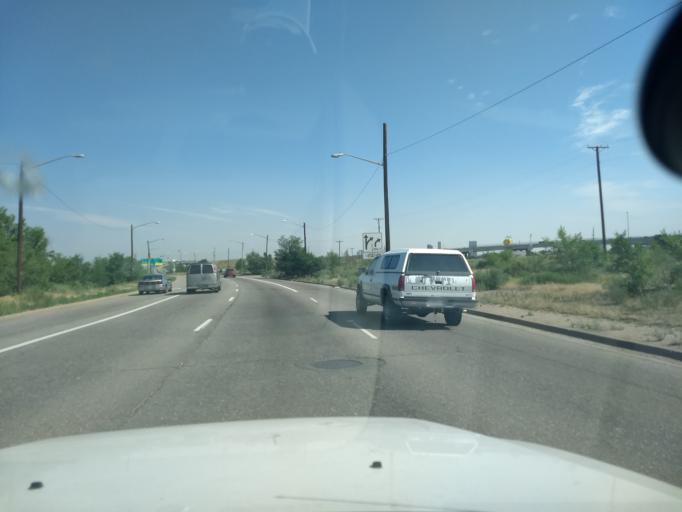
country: US
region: Colorado
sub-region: Denver County
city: Denver
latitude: 39.6991
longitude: -104.9920
